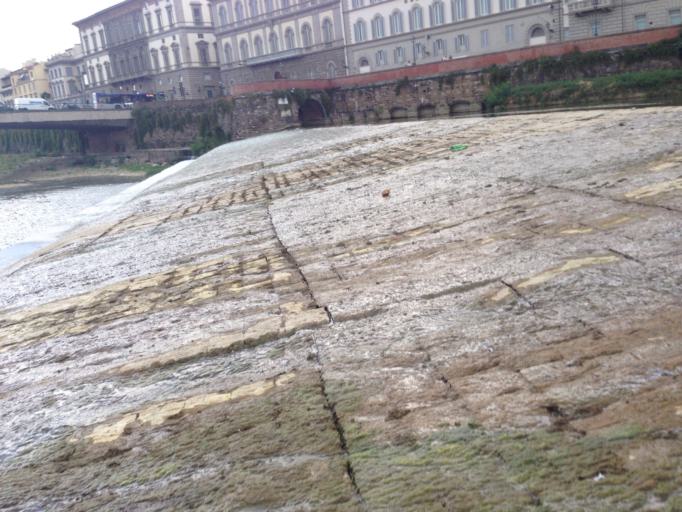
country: IT
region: Tuscany
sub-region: Province of Florence
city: Florence
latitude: 43.7716
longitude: 11.2444
